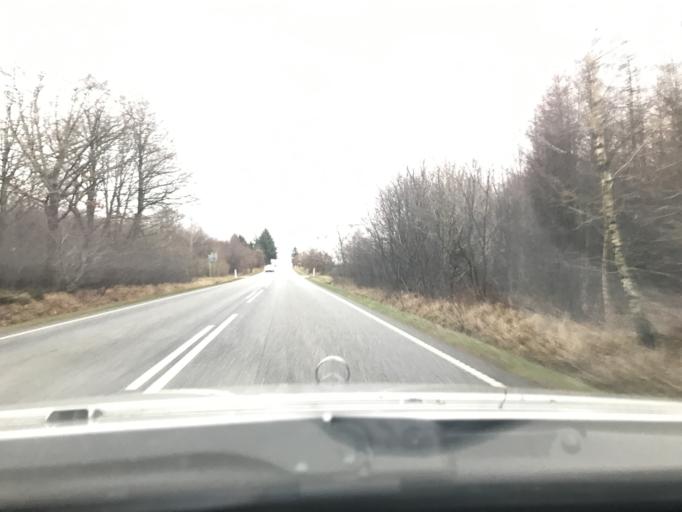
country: DK
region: South Denmark
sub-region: Tonder Kommune
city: Logumkloster
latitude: 55.1735
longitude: 8.9467
